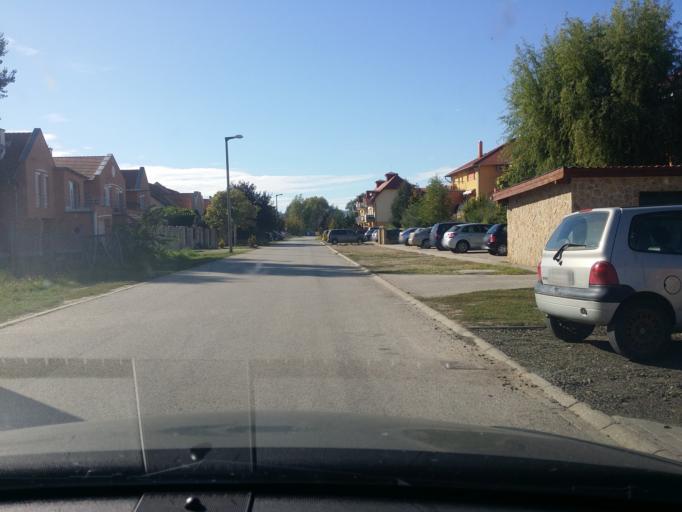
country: HU
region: Pest
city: God
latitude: 47.6927
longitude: 19.1545
